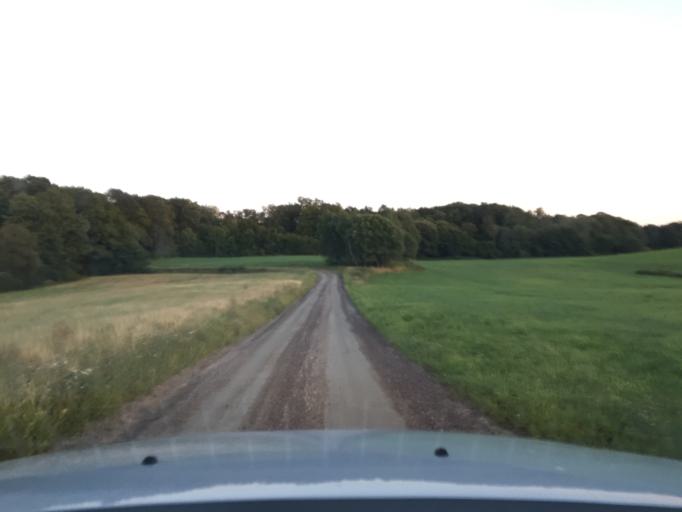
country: SE
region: Skane
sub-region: Hassleholms Kommun
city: Sosdala
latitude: 55.9931
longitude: 13.6697
